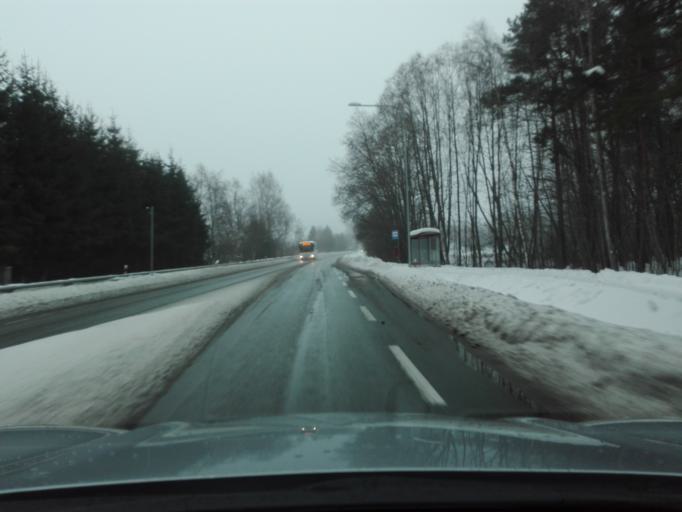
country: EE
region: Harju
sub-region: Kiili vald
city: Kiili
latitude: 59.3327
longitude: 24.7736
